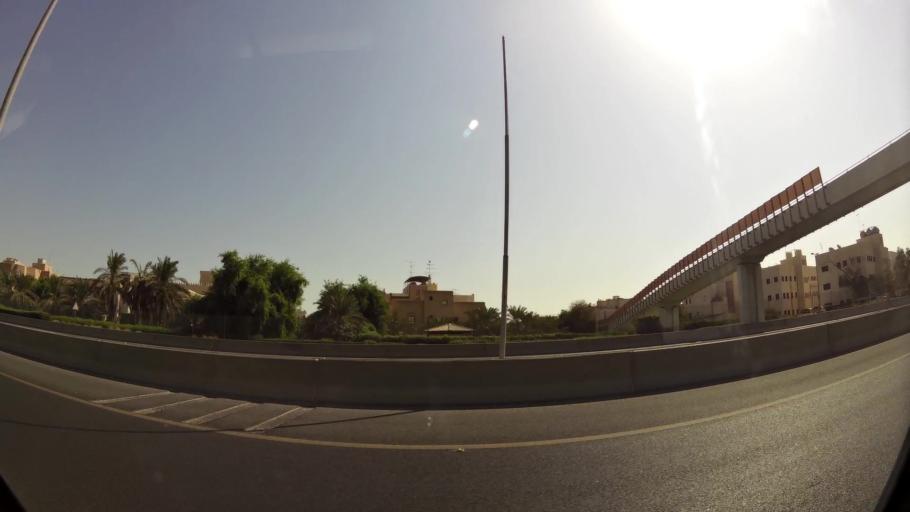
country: KW
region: Al Asimah
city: Ad Dasmah
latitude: 29.3692
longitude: 47.9951
